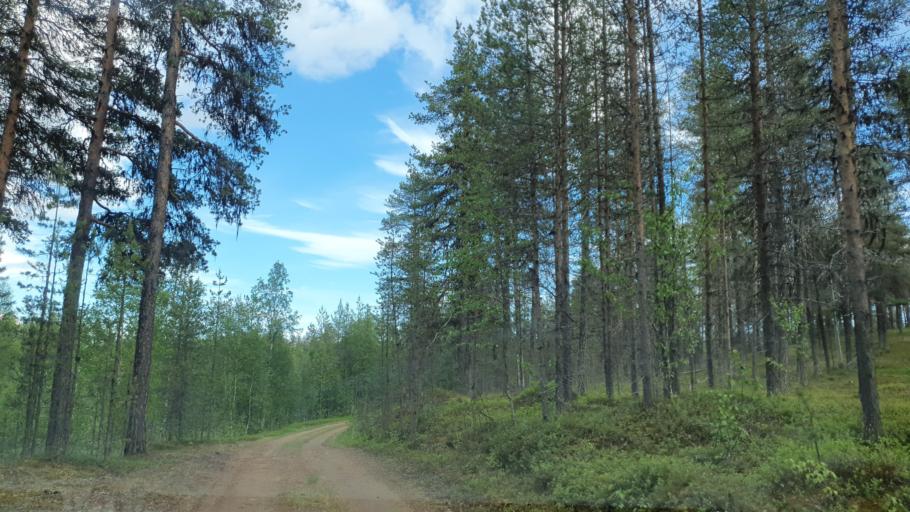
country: FI
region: Lapland
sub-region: Tunturi-Lappi
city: Kolari
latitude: 67.5359
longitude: 23.9169
